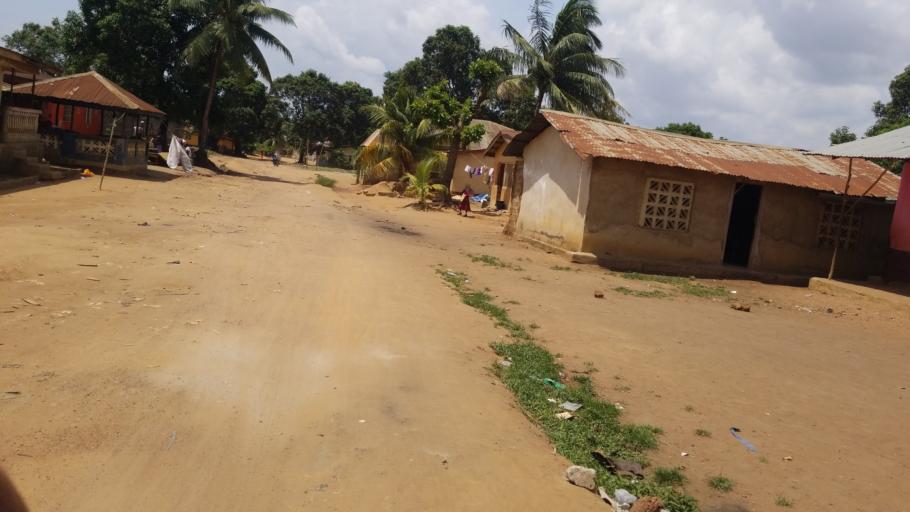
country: SL
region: Western Area
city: Waterloo
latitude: 8.3293
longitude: -13.0620
